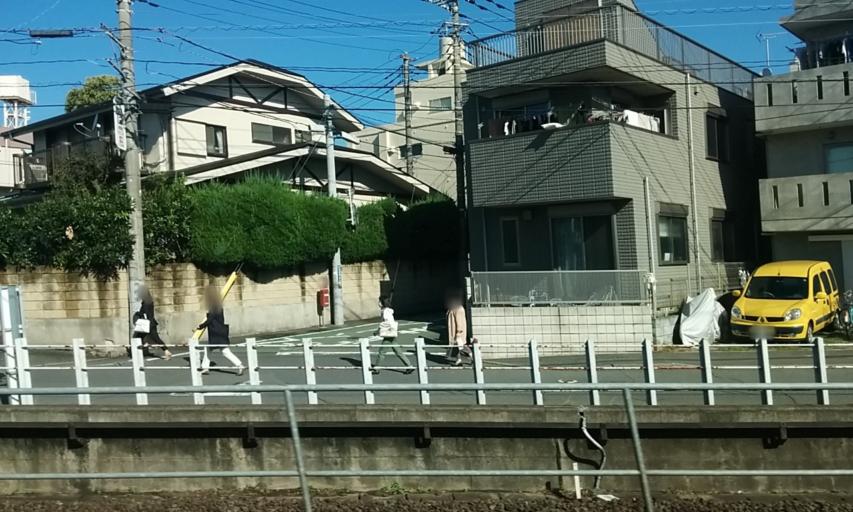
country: JP
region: Tokyo
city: Nishi-Tokyo-shi
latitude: 35.7269
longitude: 139.5357
